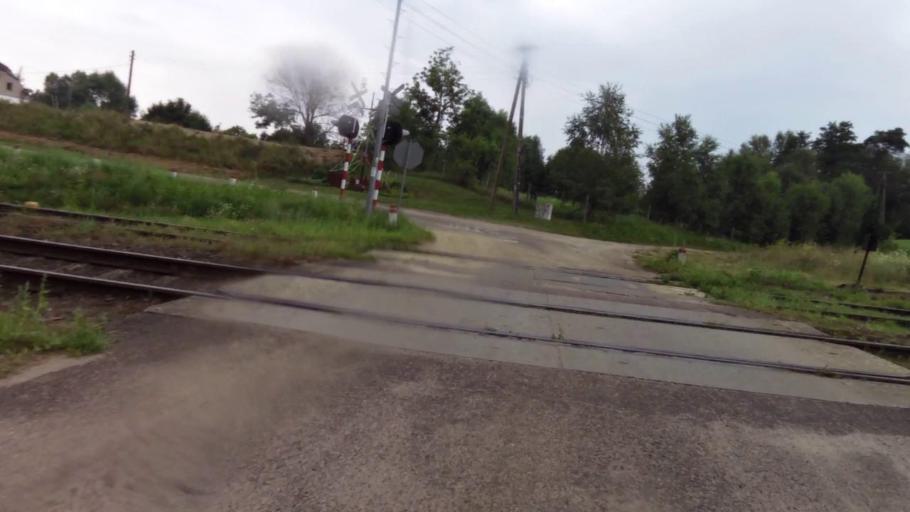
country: PL
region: West Pomeranian Voivodeship
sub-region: Powiat lobeski
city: Wegorzyno
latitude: 53.5265
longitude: 15.6494
